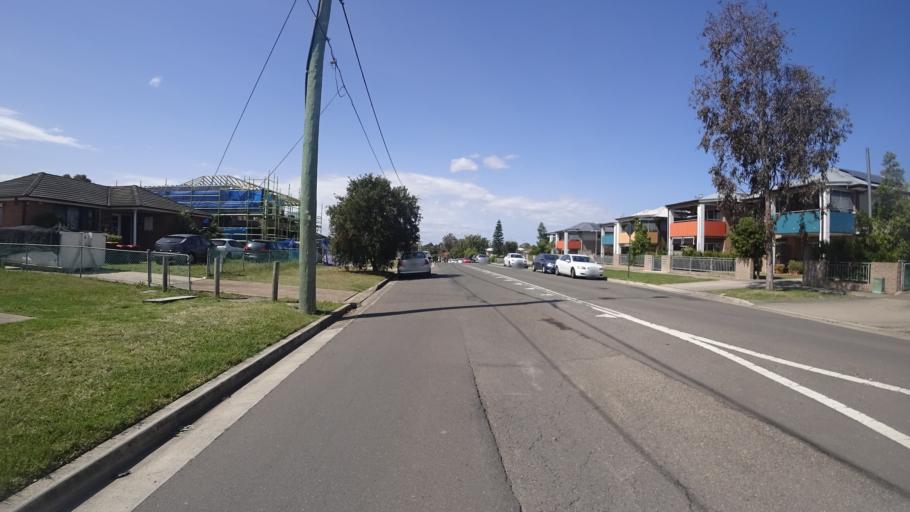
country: AU
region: New South Wales
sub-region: Liverpool
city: Miller
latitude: -33.9338
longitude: 150.8978
